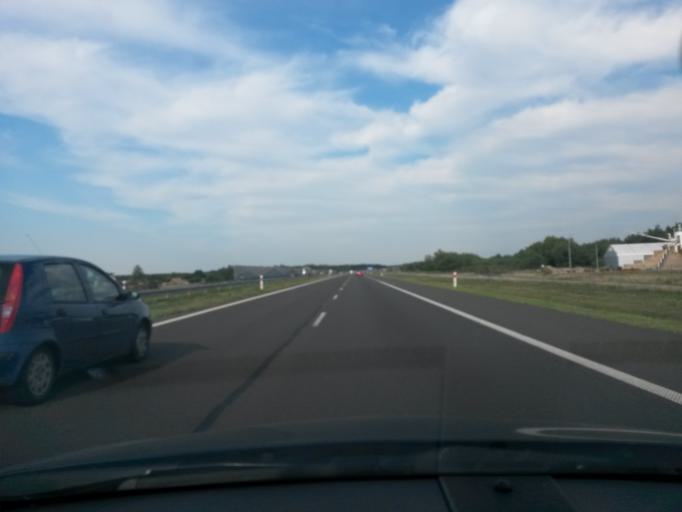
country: PL
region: Greater Poland Voivodeship
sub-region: Powiat koninski
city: Krzymow
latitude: 52.1489
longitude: 18.4364
